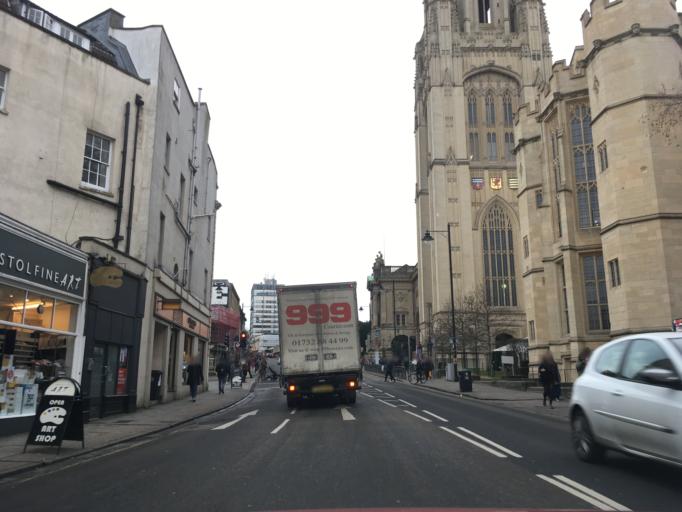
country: GB
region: England
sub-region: Bristol
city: Bristol
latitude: 51.4557
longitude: -2.6036
